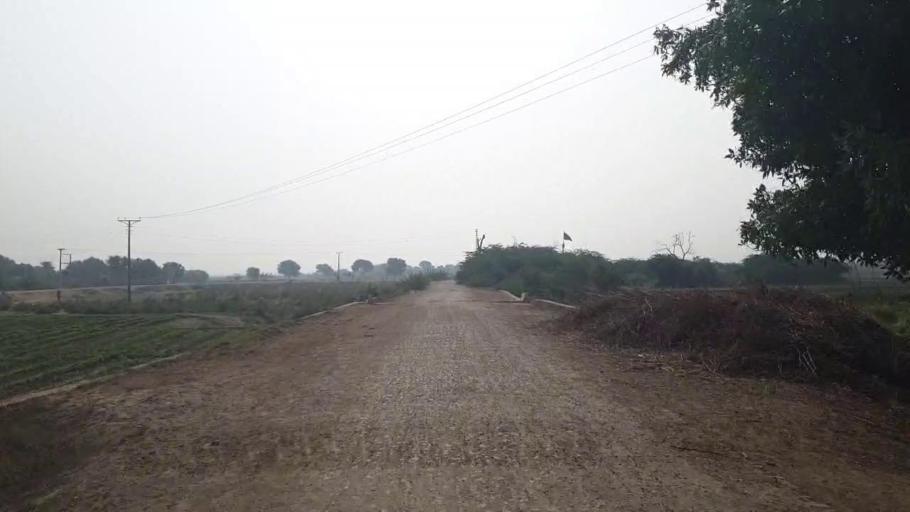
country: PK
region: Sindh
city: Tando Muhammad Khan
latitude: 25.2651
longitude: 68.5110
